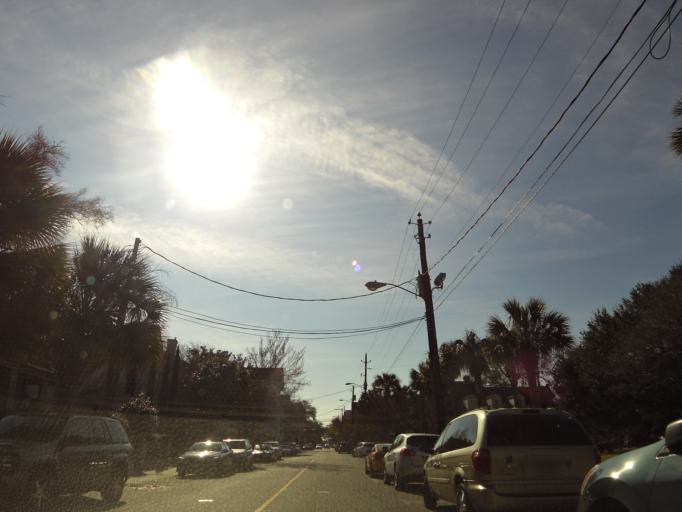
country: US
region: South Carolina
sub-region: Charleston County
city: Charleston
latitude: 32.7831
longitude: -79.9437
